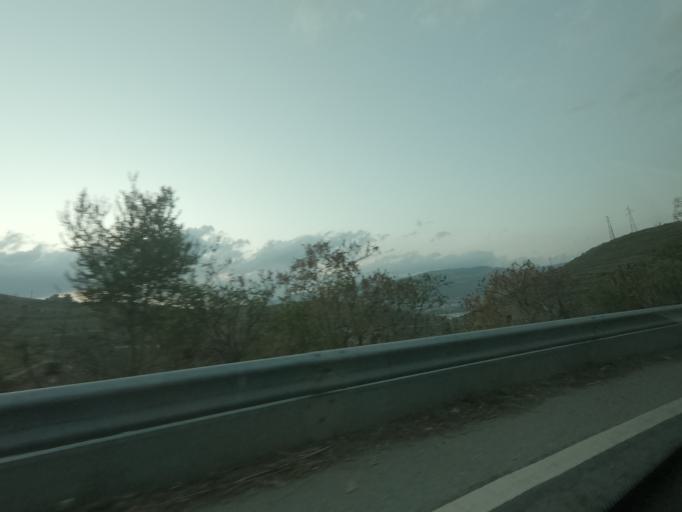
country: PT
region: Vila Real
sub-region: Peso da Regua
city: Peso da Regua
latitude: 41.1468
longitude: -7.7761
